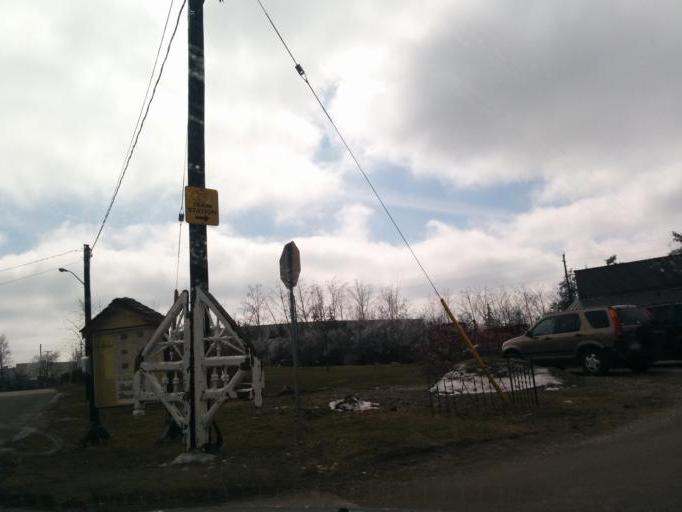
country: CA
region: Ontario
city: Waterloo
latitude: 43.5382
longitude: -80.5563
